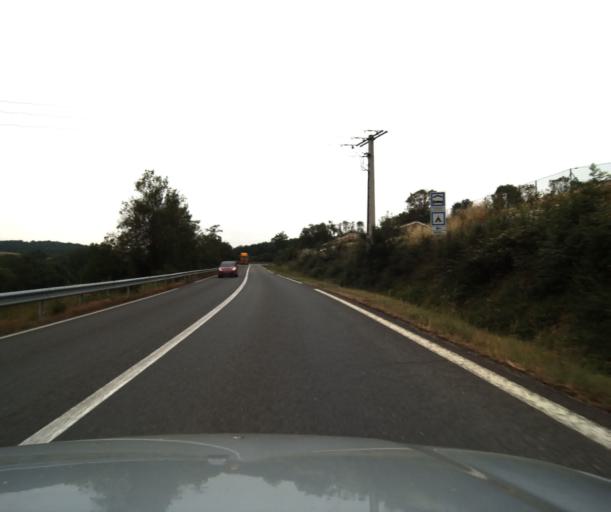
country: FR
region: Midi-Pyrenees
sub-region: Departement du Gers
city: Auch
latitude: 43.6532
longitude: 0.6215
